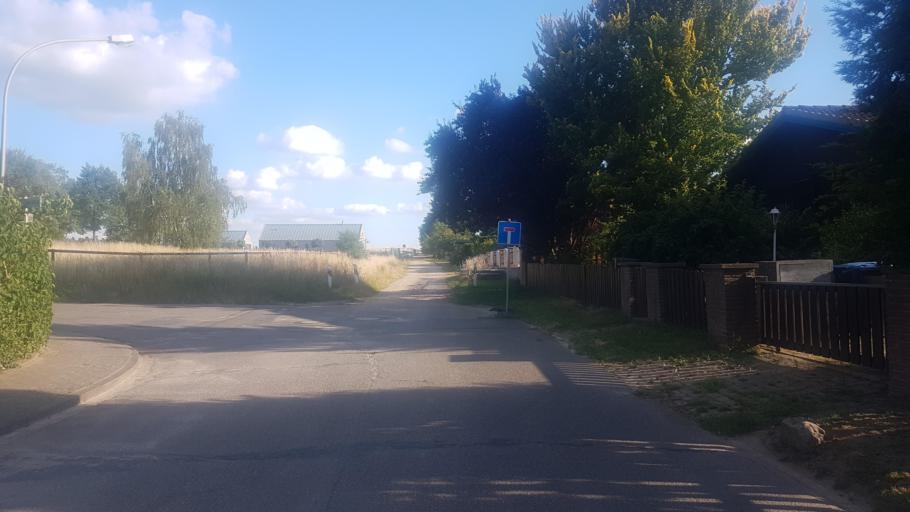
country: DE
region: Lower Saxony
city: Bleckede
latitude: 53.2618
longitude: 10.7832
